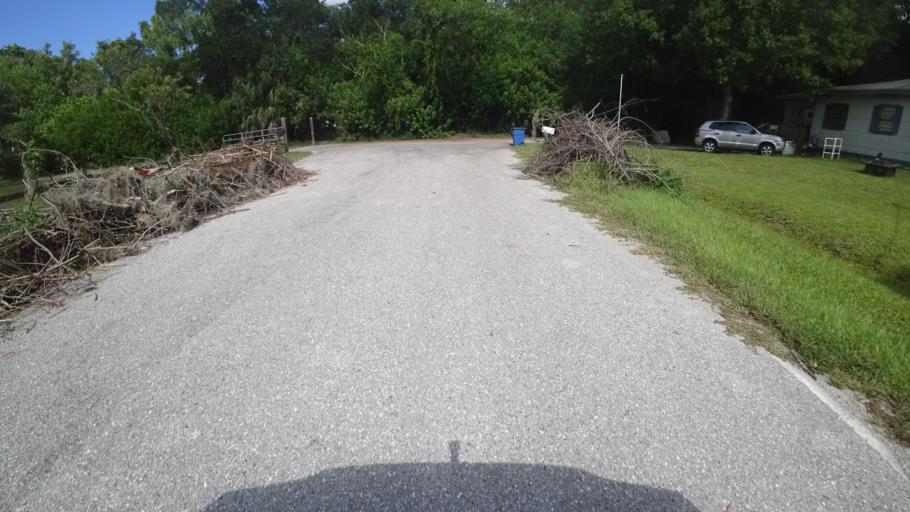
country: US
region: Florida
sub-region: Manatee County
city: Samoset
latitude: 27.4438
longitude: -82.5380
